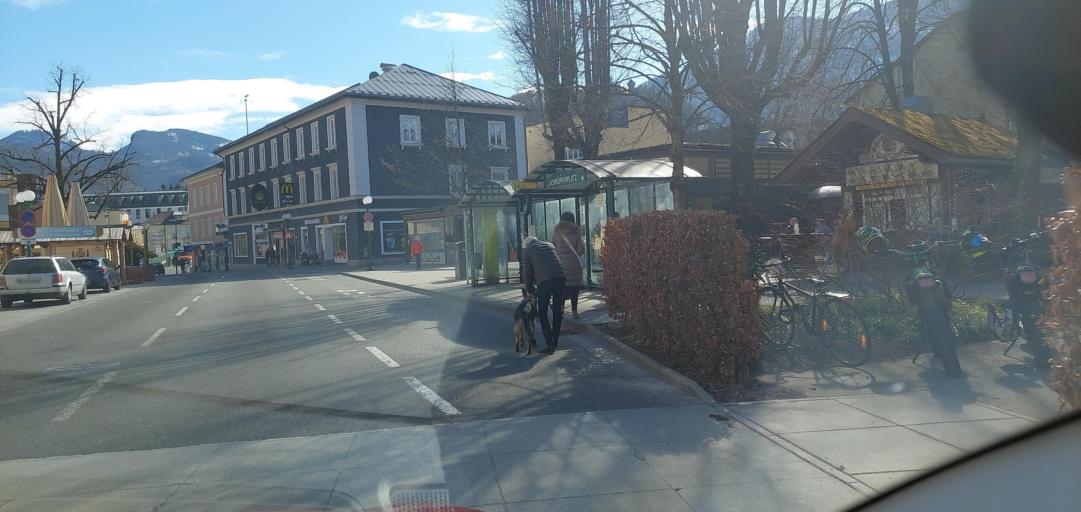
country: AT
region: Upper Austria
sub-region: Politischer Bezirk Gmunden
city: Bad Ischl
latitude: 47.7113
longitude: 13.6208
